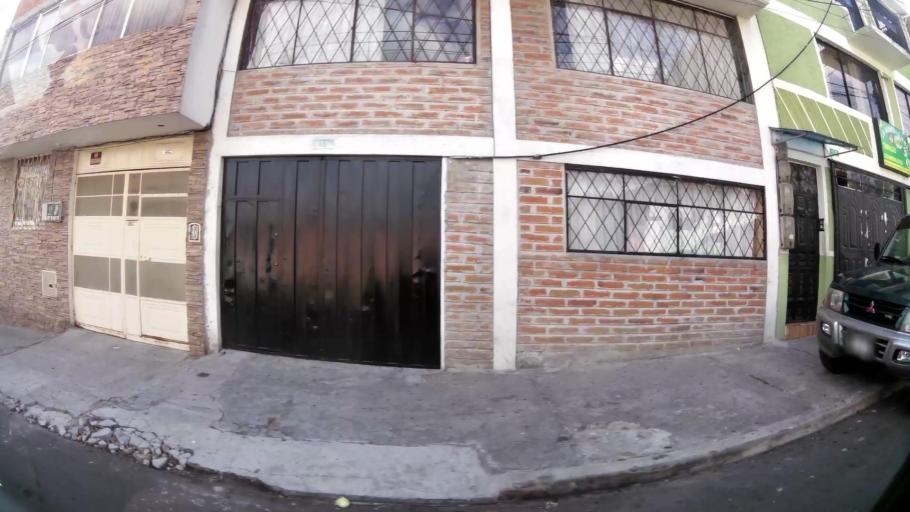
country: EC
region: Pichincha
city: Quito
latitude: -0.2285
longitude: -78.5041
